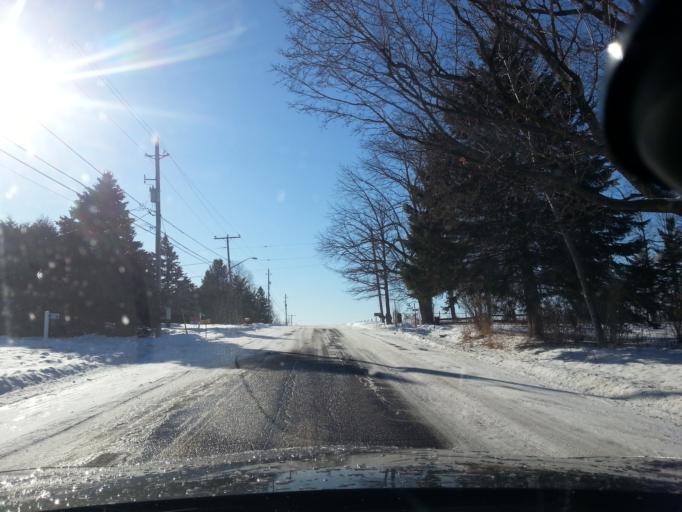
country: CA
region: Ontario
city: Clarence-Rockland
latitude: 45.3008
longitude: -75.3953
